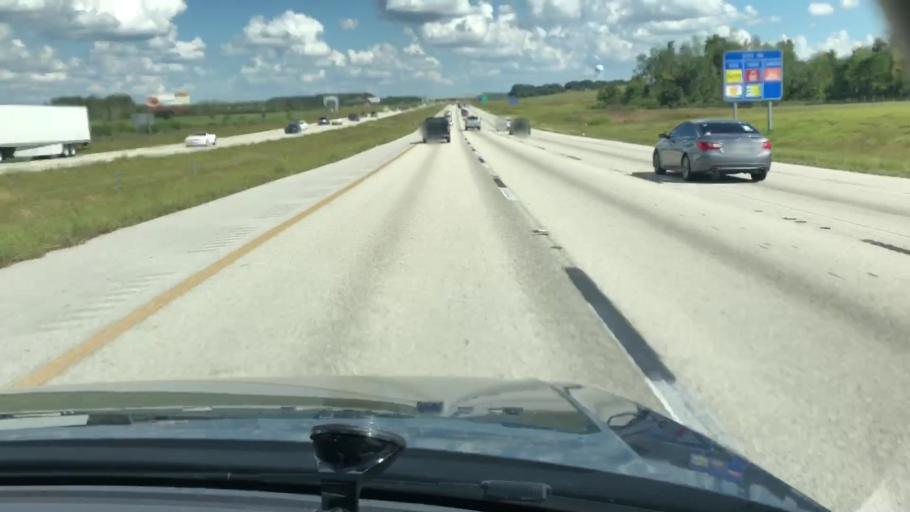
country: US
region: Florida
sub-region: Polk County
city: Polk City
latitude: 28.1574
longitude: -81.8217
